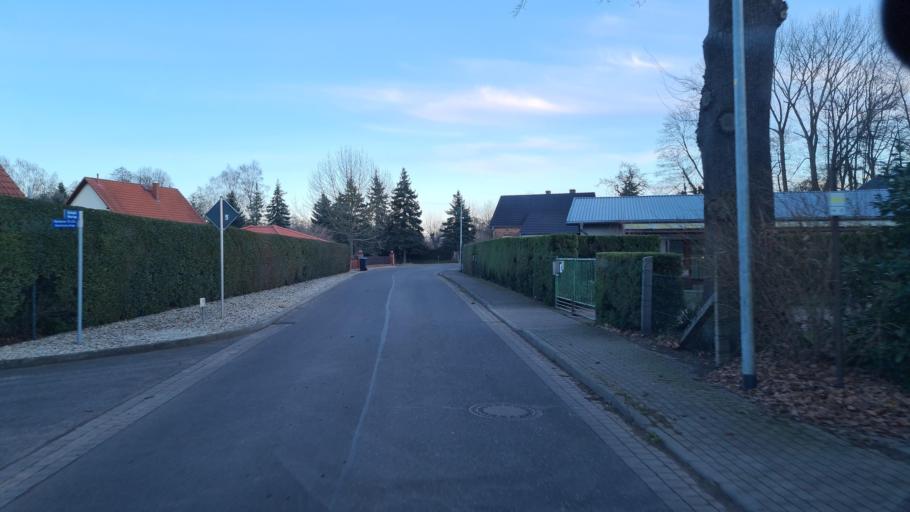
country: DE
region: Brandenburg
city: Burg
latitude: 51.8116
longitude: 14.1379
